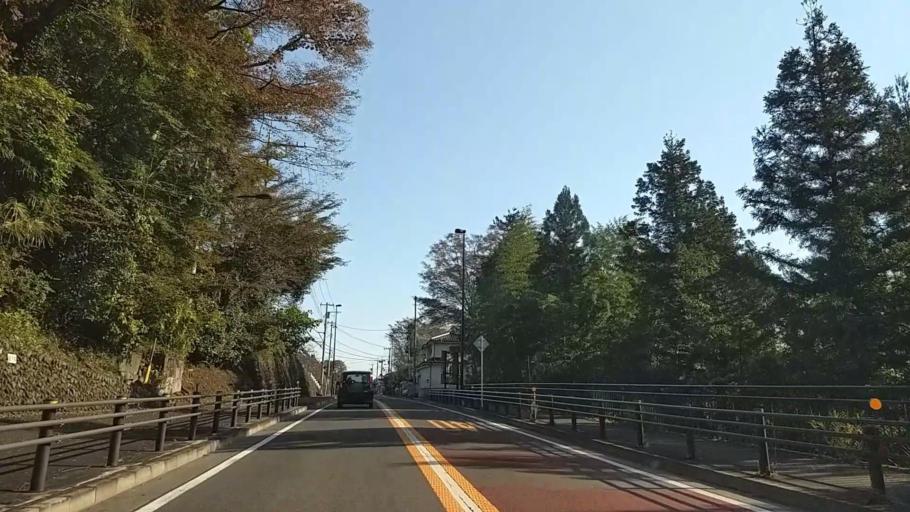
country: JP
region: Tokyo
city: Ome
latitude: 35.8063
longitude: 139.2132
